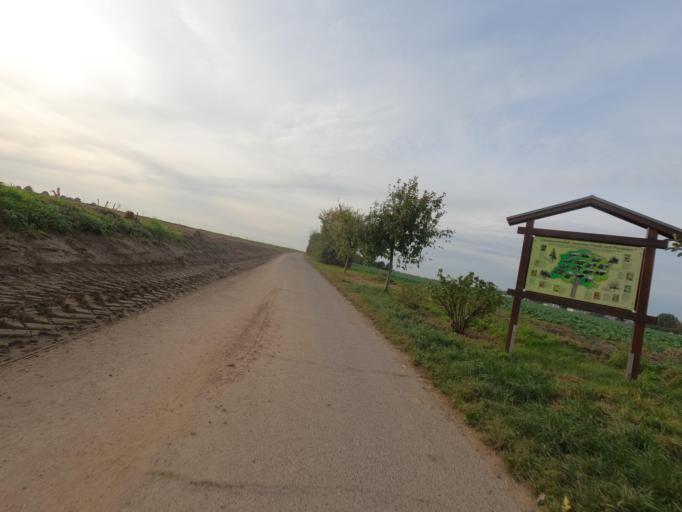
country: DE
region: North Rhine-Westphalia
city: Huckelhoven
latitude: 51.0314
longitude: 6.1733
